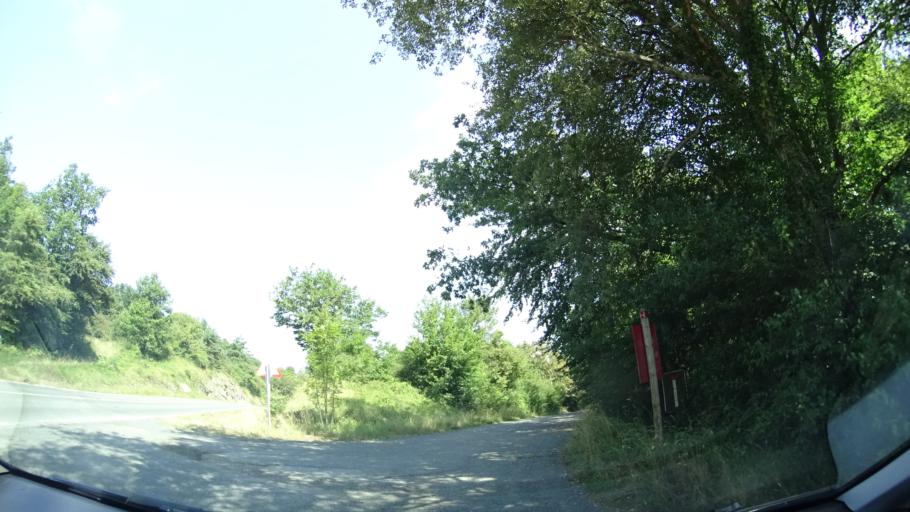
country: ES
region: Basque Country
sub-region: Provincia de Alava
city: Lezama
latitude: 42.9703
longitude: -2.9118
